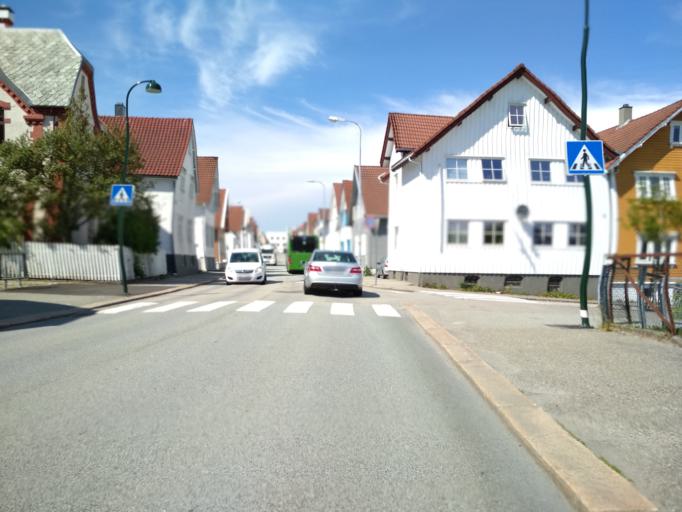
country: NO
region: Rogaland
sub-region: Stavanger
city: Stavanger
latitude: 58.9687
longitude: 5.7228
